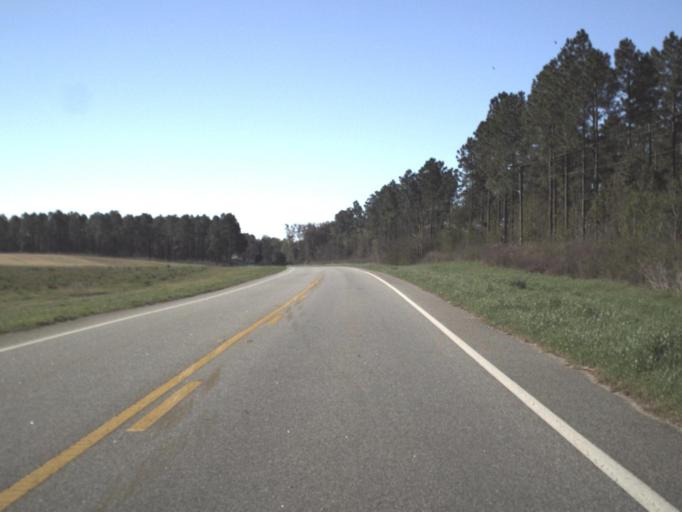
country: US
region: Georgia
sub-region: Brooks County
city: Quitman
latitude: 30.6250
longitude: -83.6467
